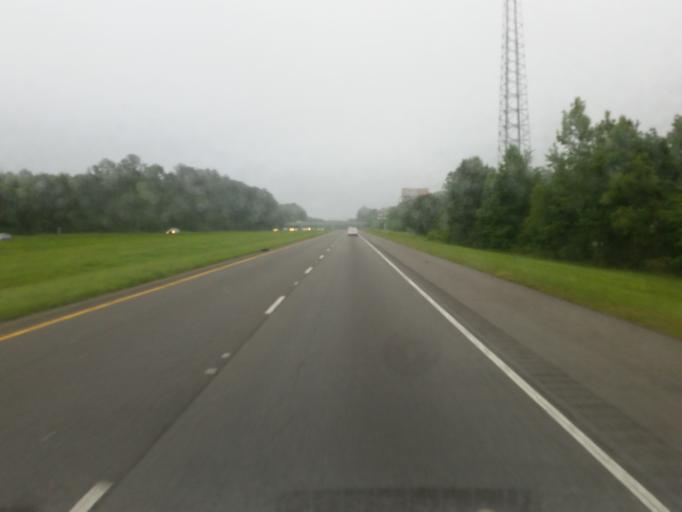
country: US
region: Louisiana
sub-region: Bossier Parish
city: Eastwood
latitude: 32.5417
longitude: -93.5447
